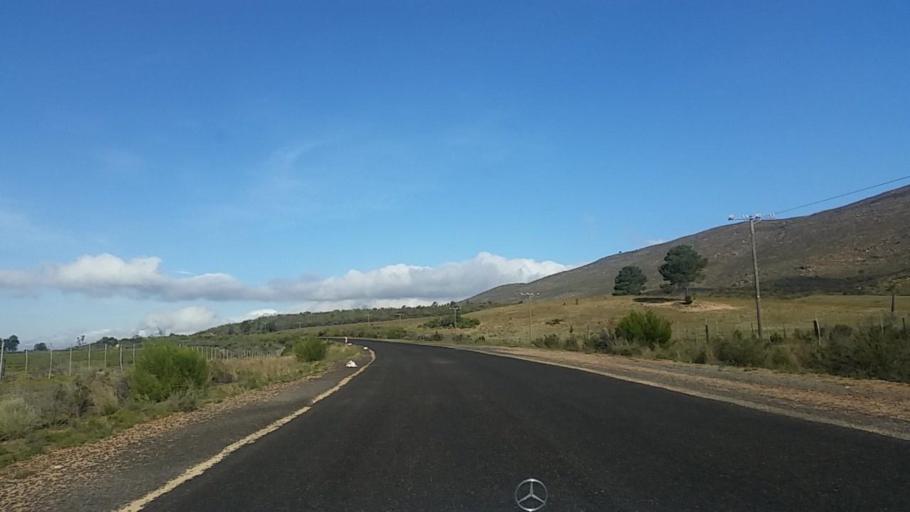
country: ZA
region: Western Cape
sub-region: Eden District Municipality
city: George
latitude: -33.8271
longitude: 22.3979
